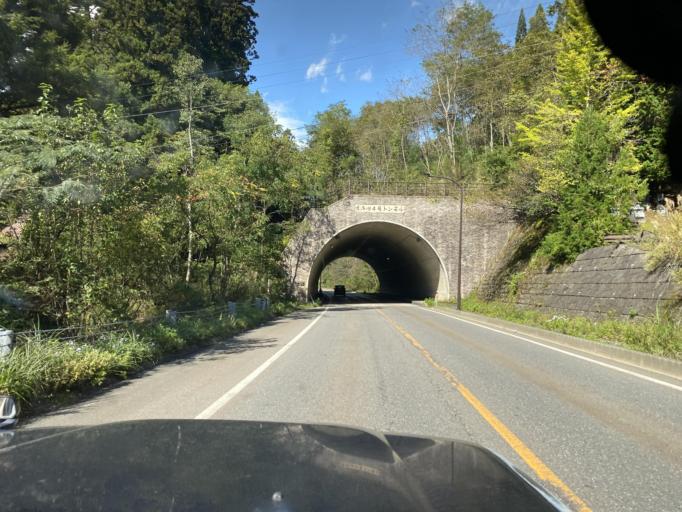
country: JP
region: Nagano
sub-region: Kitaazumi Gun
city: Hakuba
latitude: 36.6176
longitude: 137.8616
